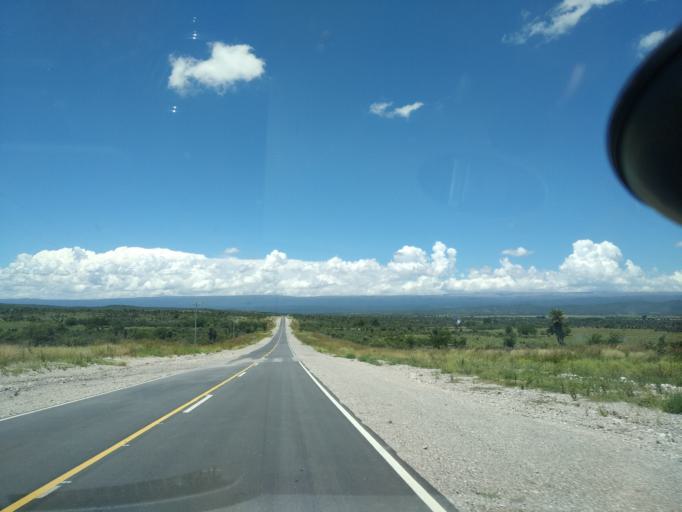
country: AR
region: Cordoba
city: Salsacate
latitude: -31.3590
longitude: -65.1721
